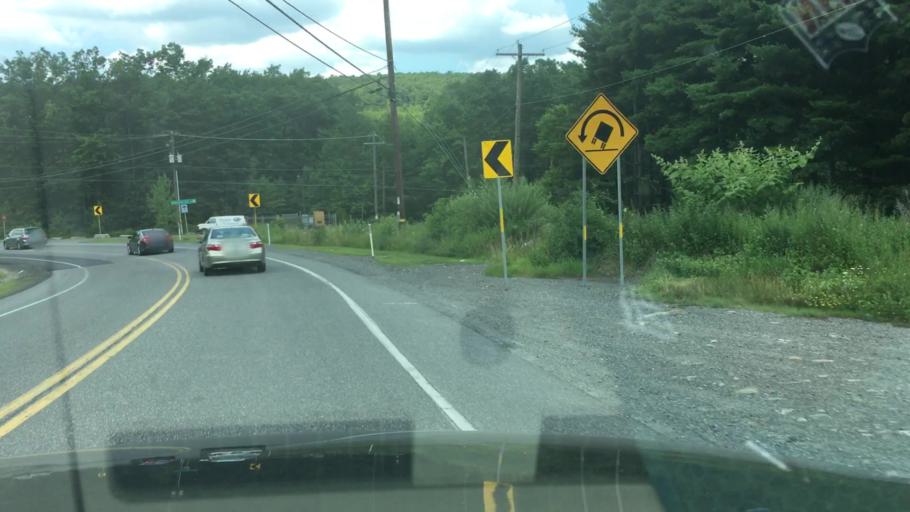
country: US
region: Pennsylvania
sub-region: Schuylkill County
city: Minersville
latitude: 40.7092
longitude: -76.3304
